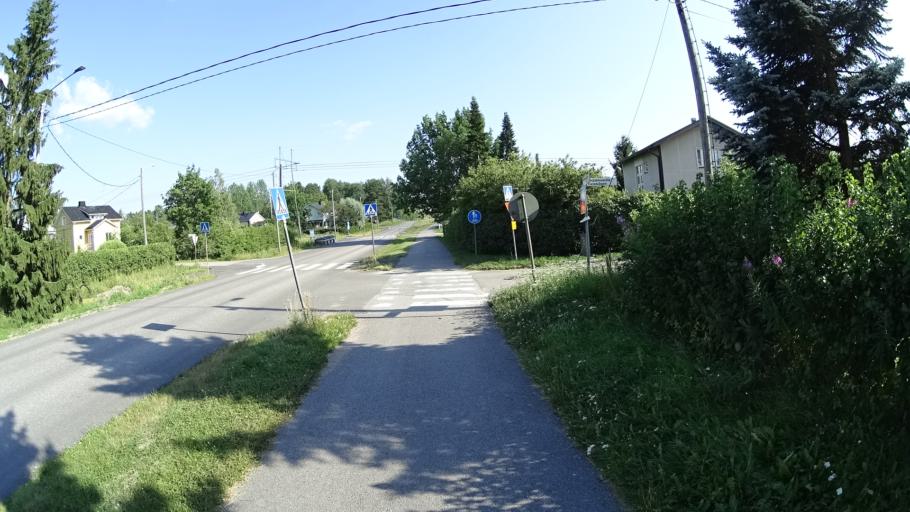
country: FI
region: Uusimaa
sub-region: Porvoo
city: Porvoo
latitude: 60.4056
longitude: 25.6493
